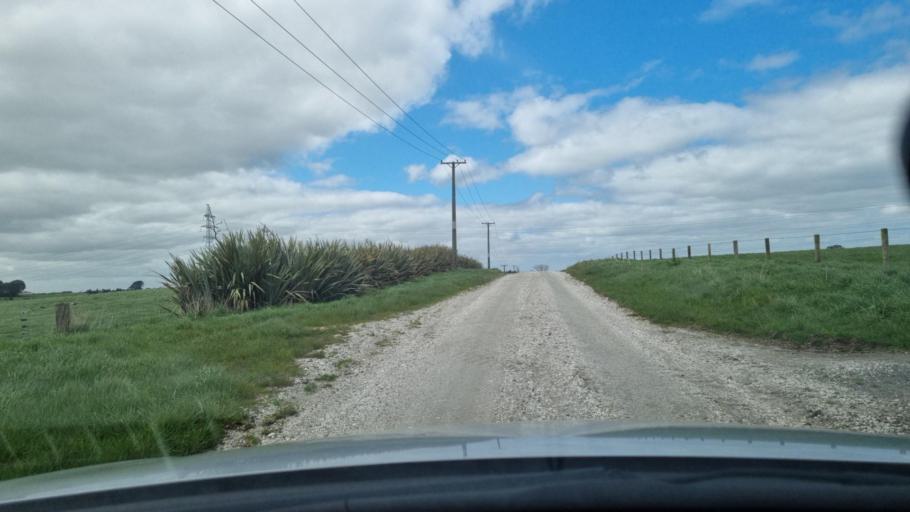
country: NZ
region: Southland
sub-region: Invercargill City
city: Invercargill
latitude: -46.4427
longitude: 168.4486
